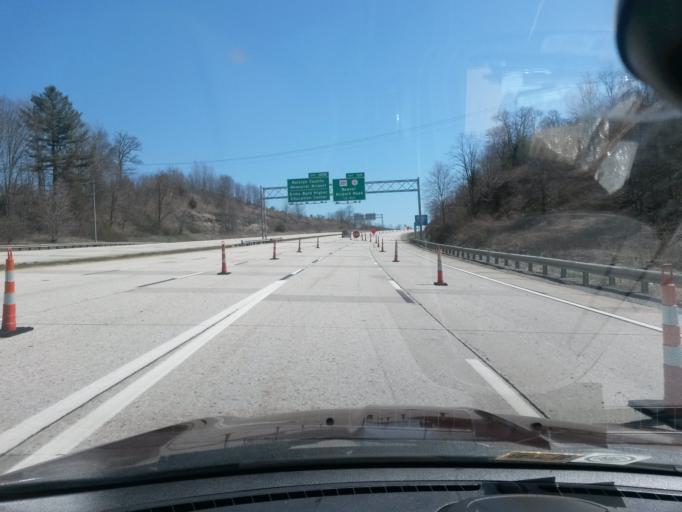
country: US
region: West Virginia
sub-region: Raleigh County
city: Beaver
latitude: 37.7649
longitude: -81.1415
